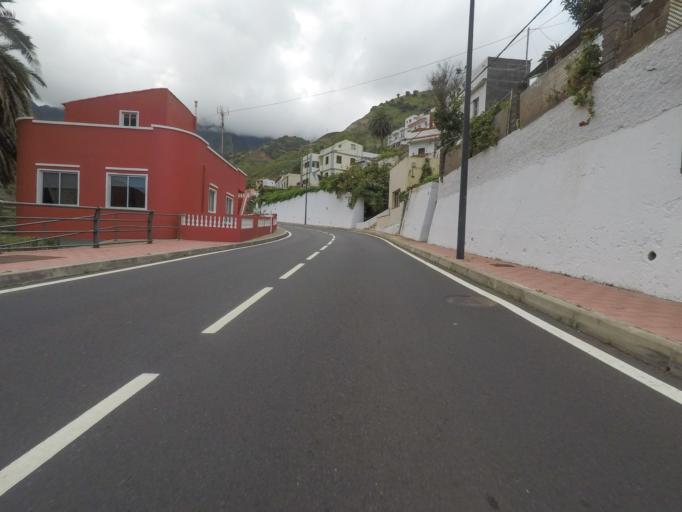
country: ES
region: Canary Islands
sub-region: Provincia de Santa Cruz de Tenerife
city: Hermigua
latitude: 28.1502
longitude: -17.1982
